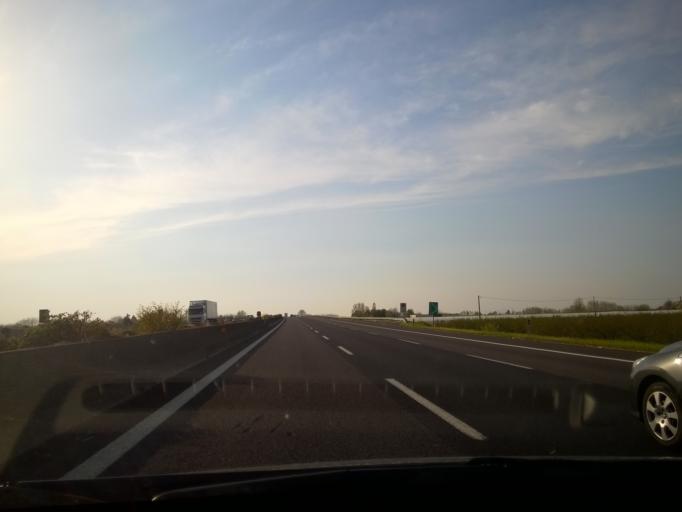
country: IT
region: Emilia-Romagna
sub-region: Provincia di Ravenna
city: Granarolo
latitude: 44.3059
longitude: 11.9479
